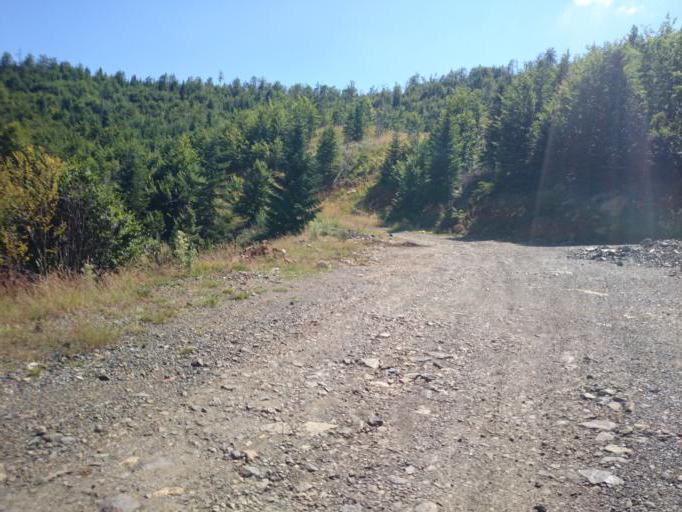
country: AL
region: Diber
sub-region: Rrethi i Bulqizes
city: Zerqan
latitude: 41.4175
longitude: 20.3240
